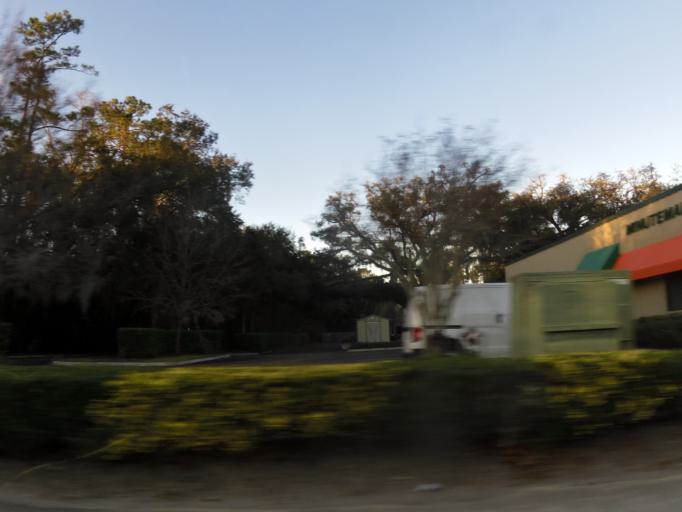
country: US
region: Florida
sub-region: Saint Johns County
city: Fruit Cove
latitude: 30.2059
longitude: -81.6074
